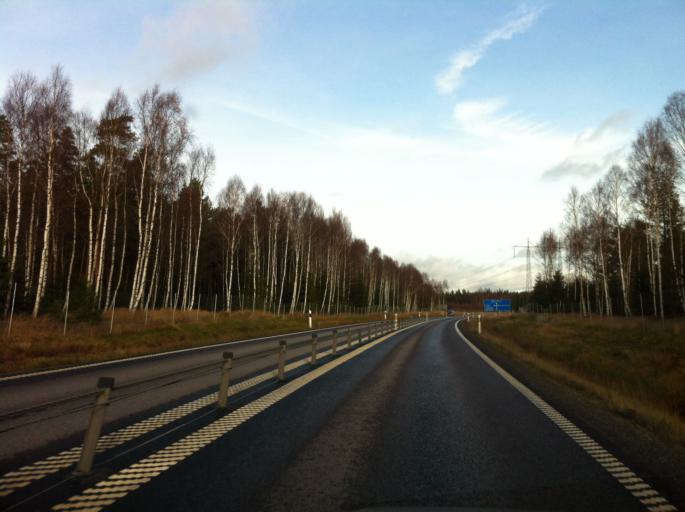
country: SE
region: Kronoberg
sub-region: Almhults Kommun
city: AElmhult
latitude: 56.6203
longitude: 14.2413
